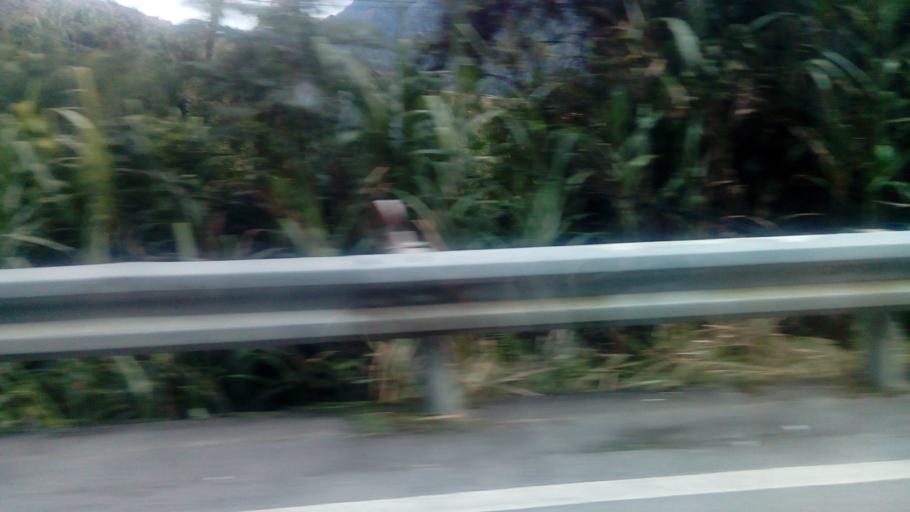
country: TW
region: Taiwan
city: Daxi
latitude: 24.4566
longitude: 121.3936
